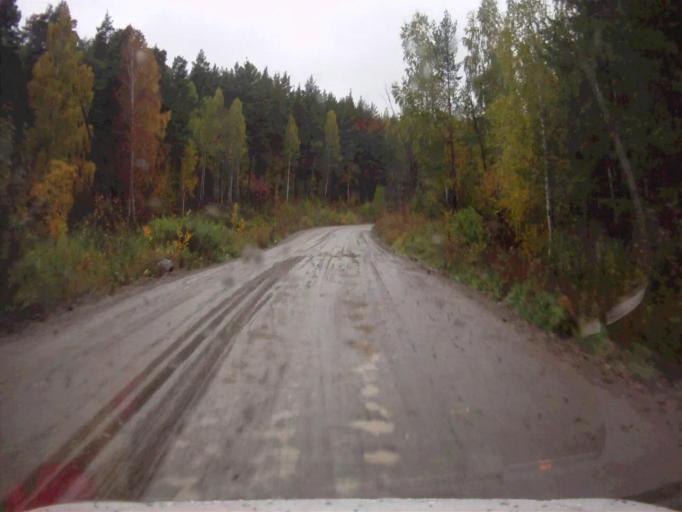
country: RU
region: Chelyabinsk
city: Kyshtym
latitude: 55.7419
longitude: 60.4974
